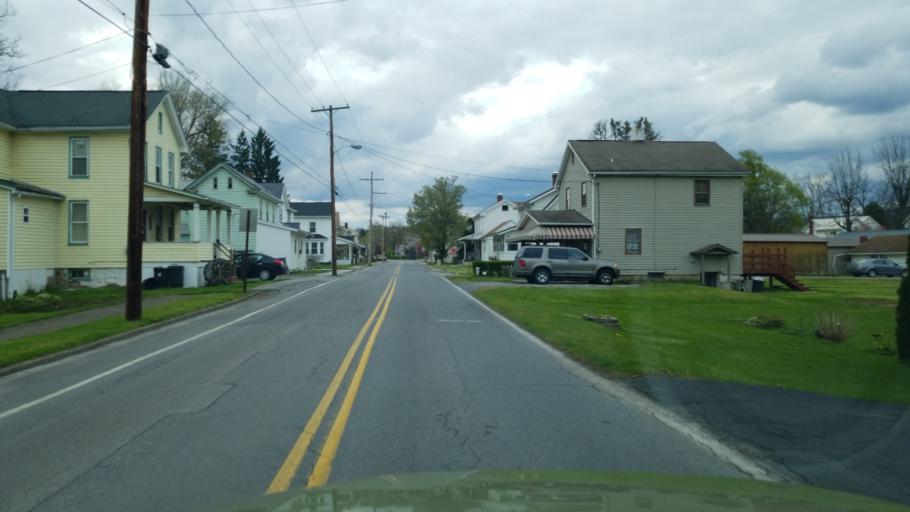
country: US
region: Pennsylvania
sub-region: Blair County
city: Hollidaysburg
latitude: 40.4220
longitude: -78.3939
